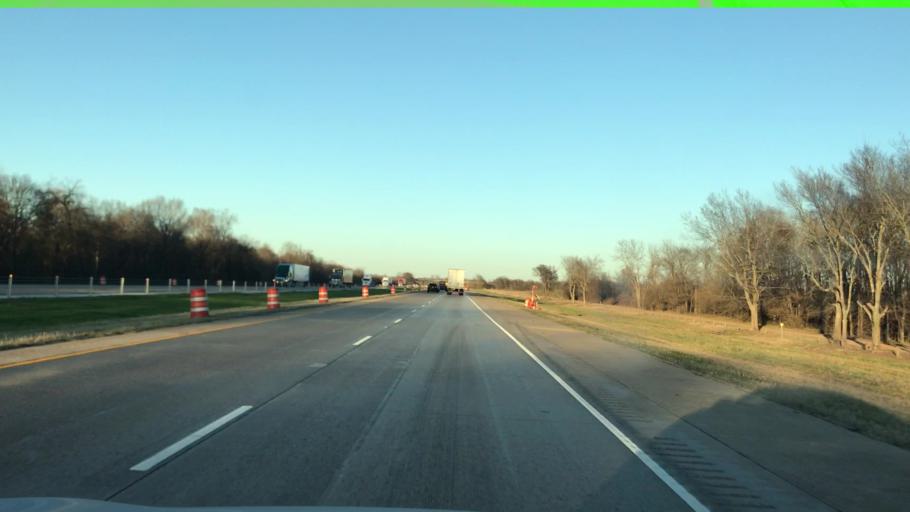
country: US
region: Arkansas
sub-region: Miller County
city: Texarkana
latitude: 33.5671
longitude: -93.8538
